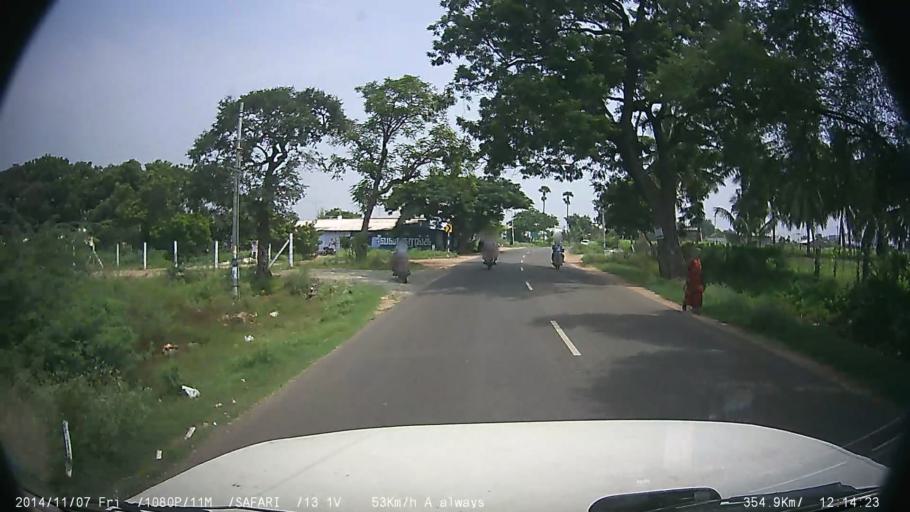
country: IN
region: Tamil Nadu
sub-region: Tiruppur
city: Tiruppur
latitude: 11.1026
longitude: 77.2837
